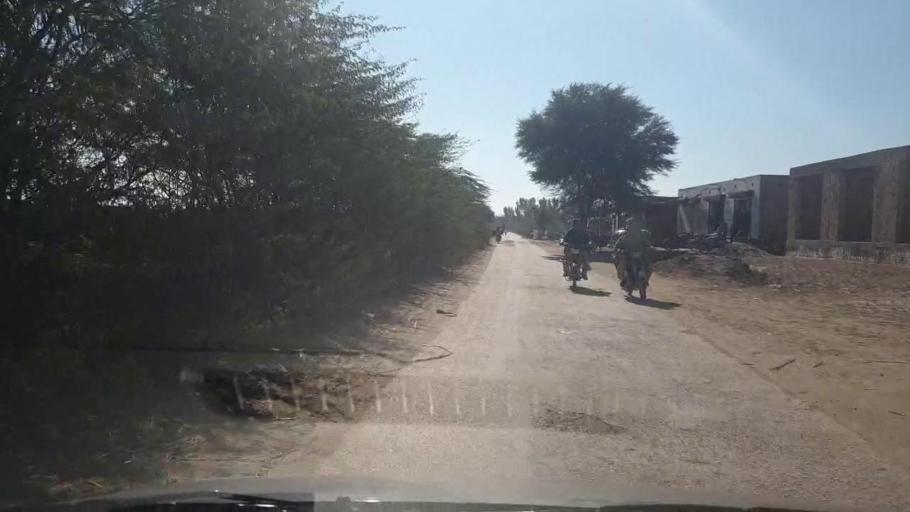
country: PK
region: Sindh
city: Bozdar
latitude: 27.1801
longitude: 68.6394
